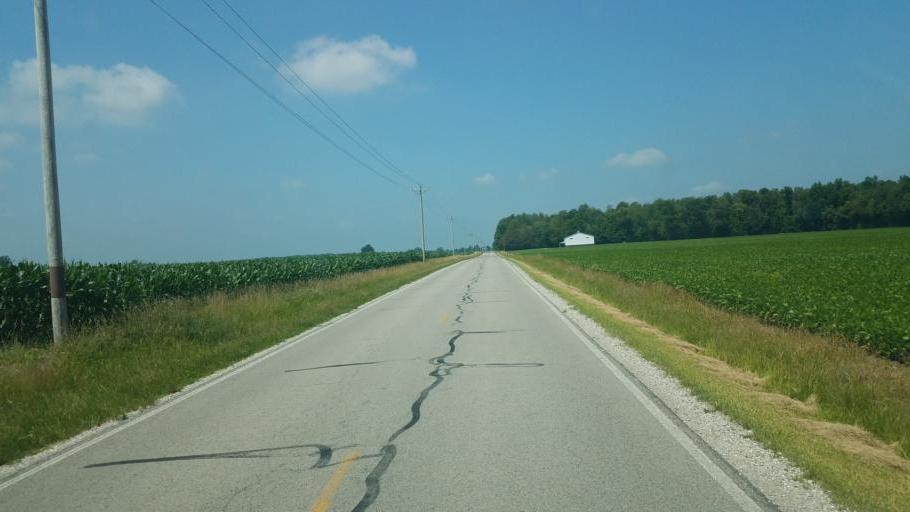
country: US
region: Ohio
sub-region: Huron County
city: Willard
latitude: 40.9937
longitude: -82.8897
